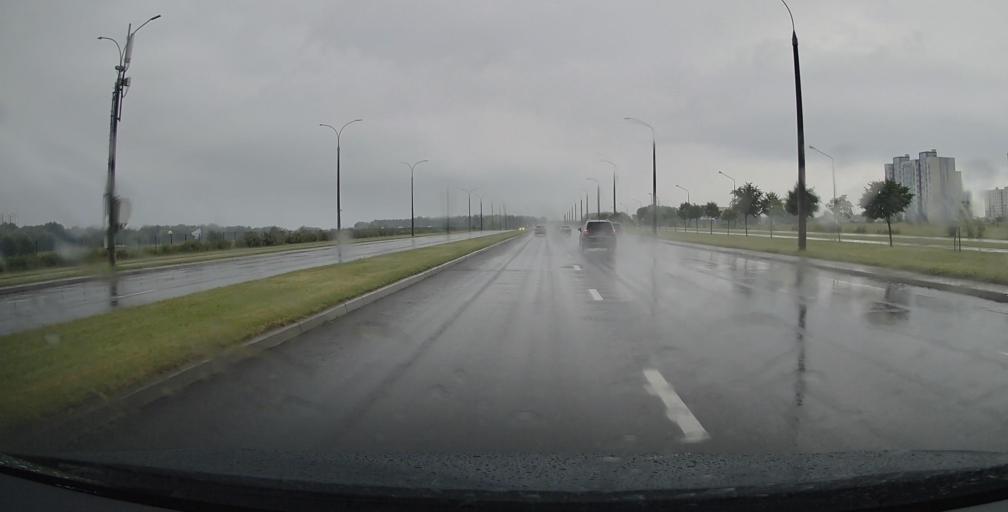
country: BY
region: Brest
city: Brest
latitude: 52.0828
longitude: 23.7604
